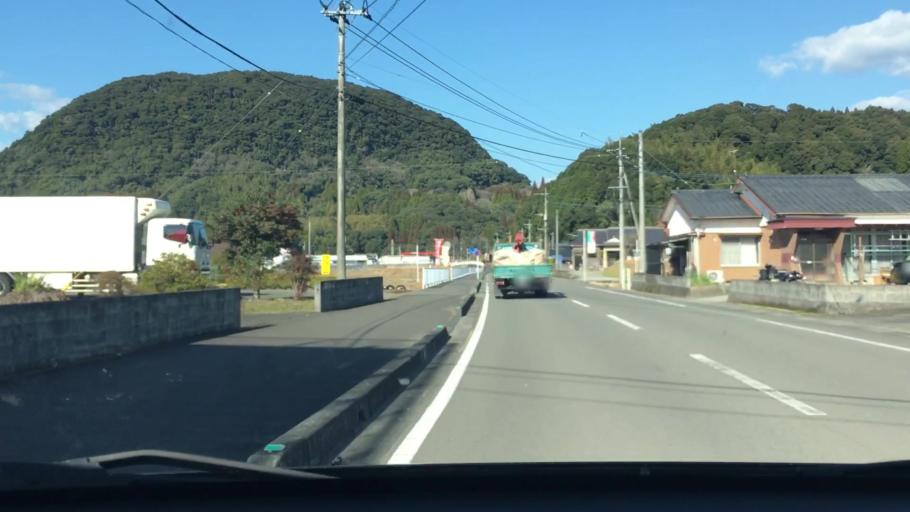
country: JP
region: Kagoshima
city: Satsumasendai
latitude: 31.7933
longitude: 130.4103
